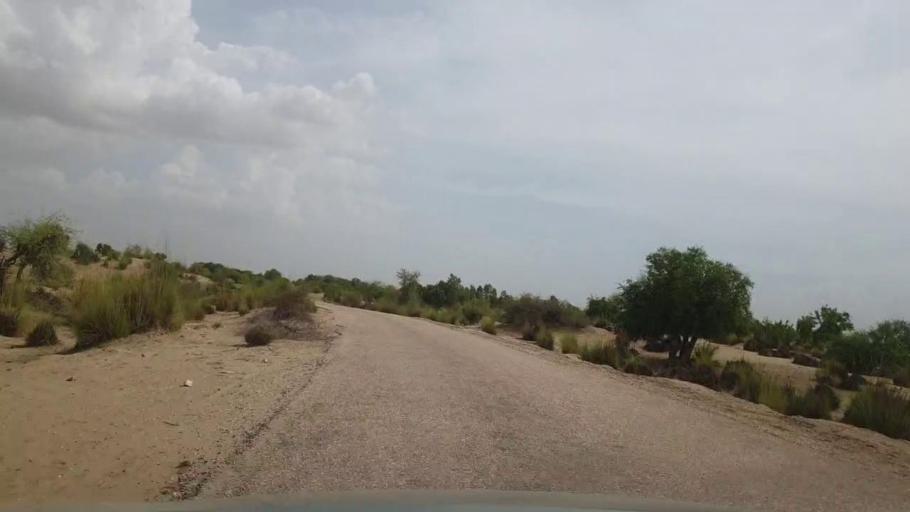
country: PK
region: Sindh
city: Bozdar
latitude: 27.0866
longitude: 69.0135
